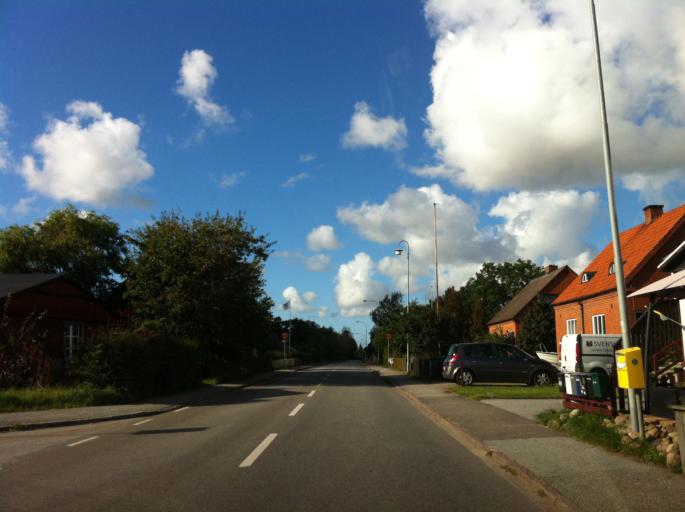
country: SE
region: Skane
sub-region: Svalovs Kommun
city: Teckomatorp
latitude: 55.8304
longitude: 13.0306
